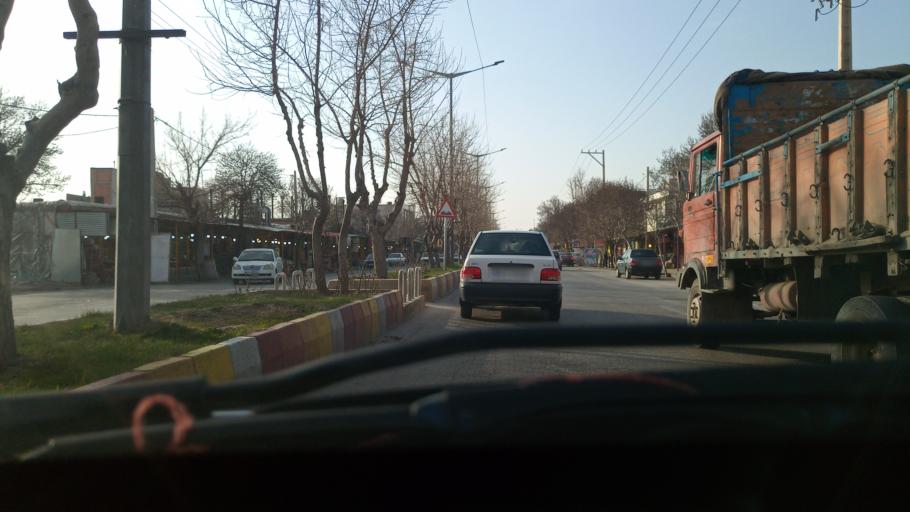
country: IR
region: Khorasan-e Shomali
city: Faruj
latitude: 37.2307
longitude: 58.2214
